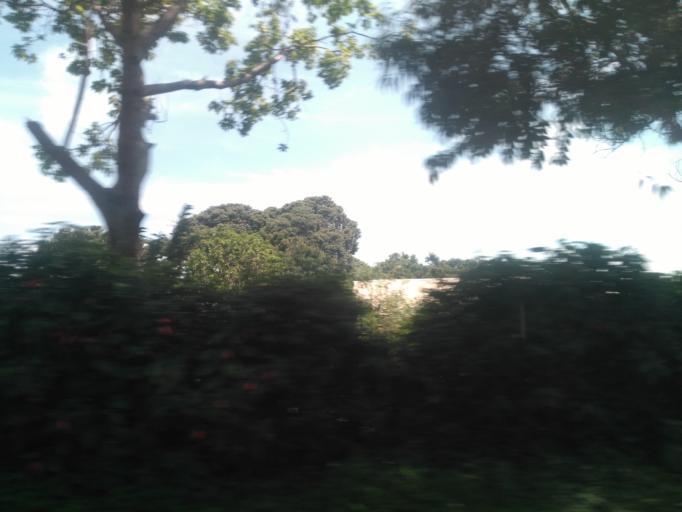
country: UG
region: Central Region
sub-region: Wakiso District
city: Entebbe
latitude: 0.0469
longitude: 32.4653
